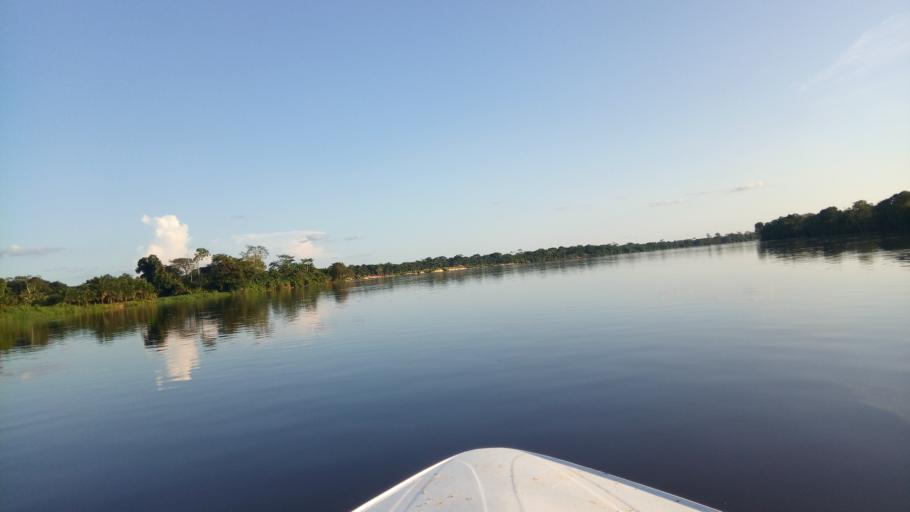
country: CD
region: Eastern Province
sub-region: Sous-Region de la Tshopo
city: Yangambi
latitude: 0.1573
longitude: 24.0520
